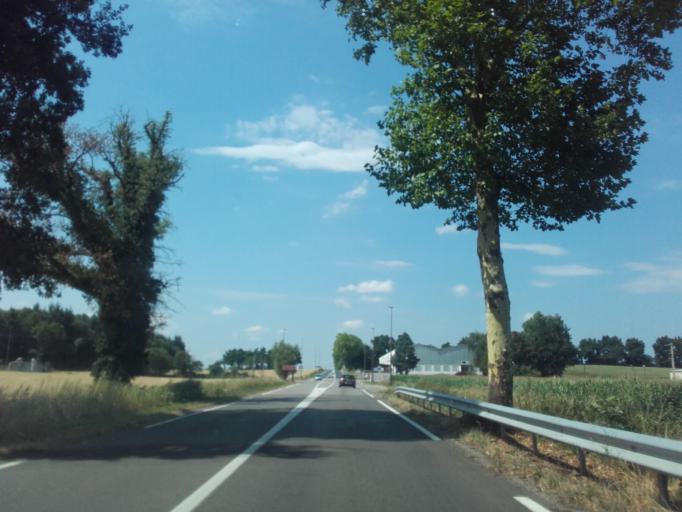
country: FR
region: Rhone-Alpes
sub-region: Departement de l'Ain
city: Perouges
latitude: 45.9375
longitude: 5.1810
